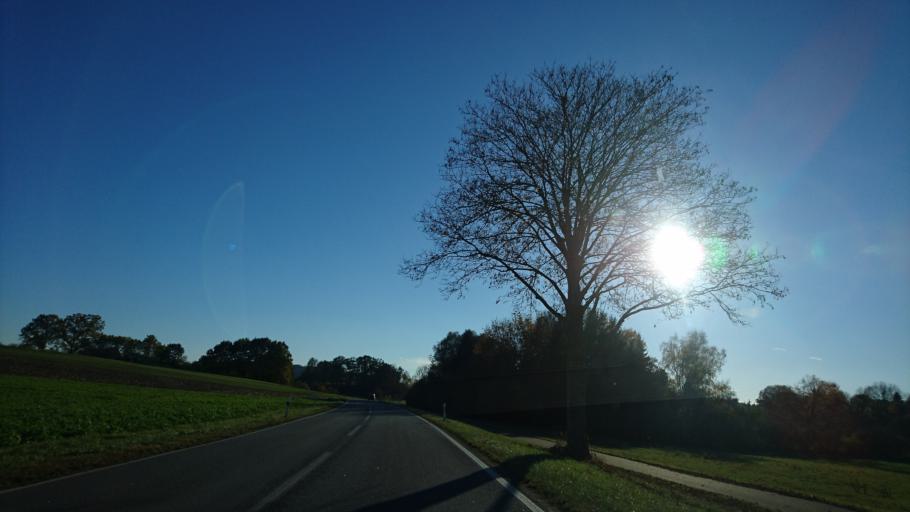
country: DE
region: Bavaria
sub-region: Swabia
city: Dinkelscherben
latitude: 48.3628
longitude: 10.5740
